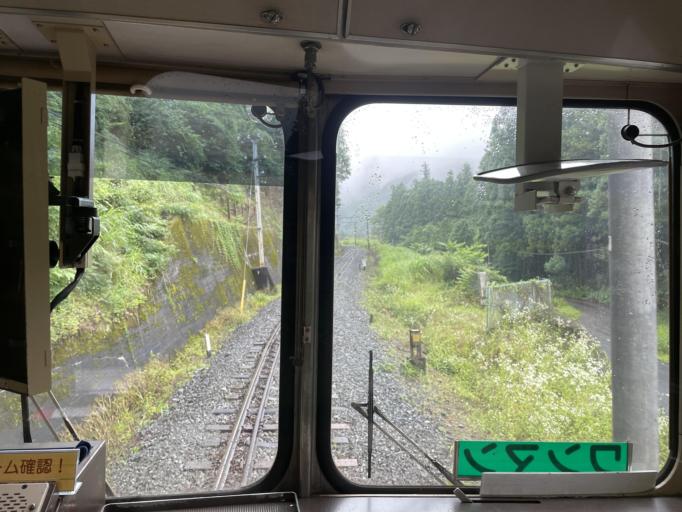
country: JP
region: Saitama
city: Chichibu
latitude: 35.9569
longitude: 139.0035
